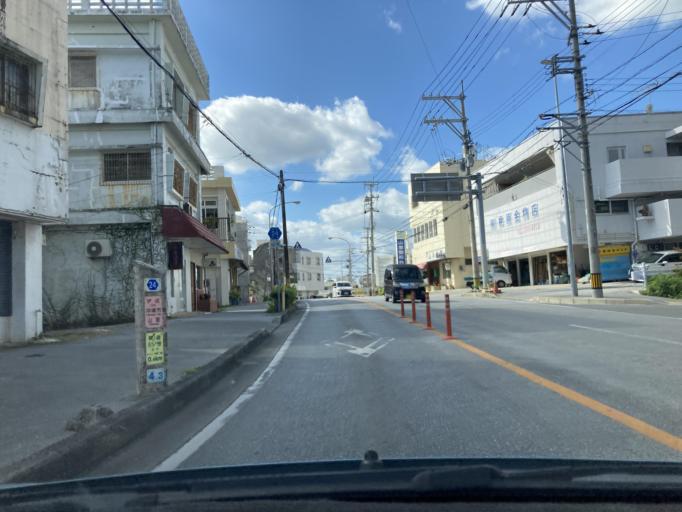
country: JP
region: Okinawa
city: Okinawa
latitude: 26.3233
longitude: 127.7929
